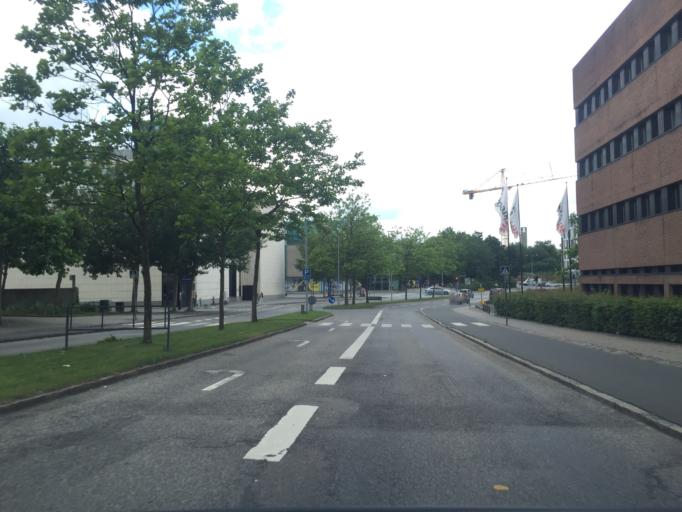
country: DK
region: Capital Region
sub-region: Lyngby-Tarbaek Kommune
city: Kongens Lyngby
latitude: 55.7711
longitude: 12.5094
